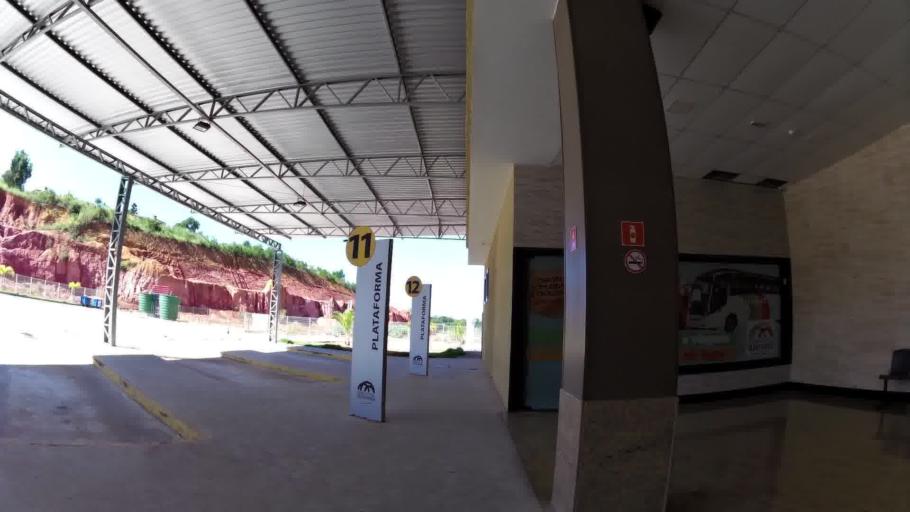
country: BR
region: Espirito Santo
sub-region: Serra
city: Serra
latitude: -20.1587
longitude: -40.1956
